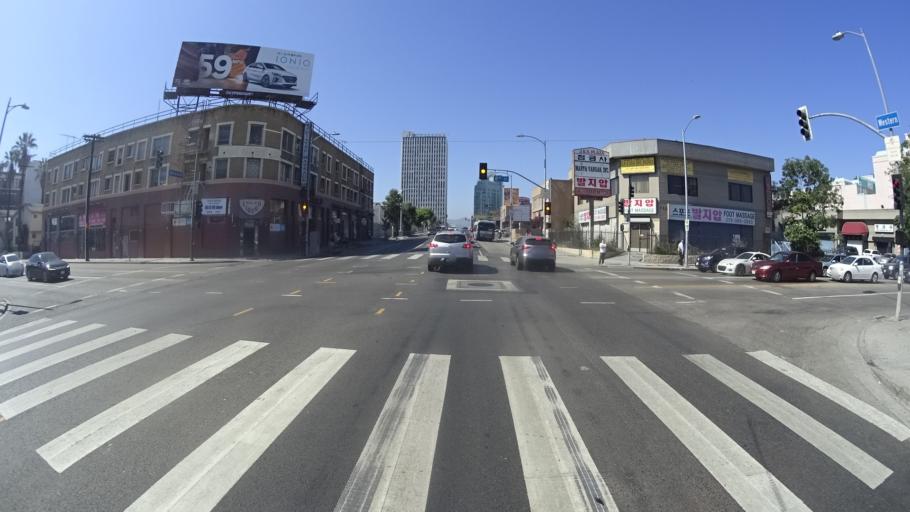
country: US
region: California
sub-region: Los Angeles County
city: Hollywood
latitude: 34.0579
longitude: -118.3090
